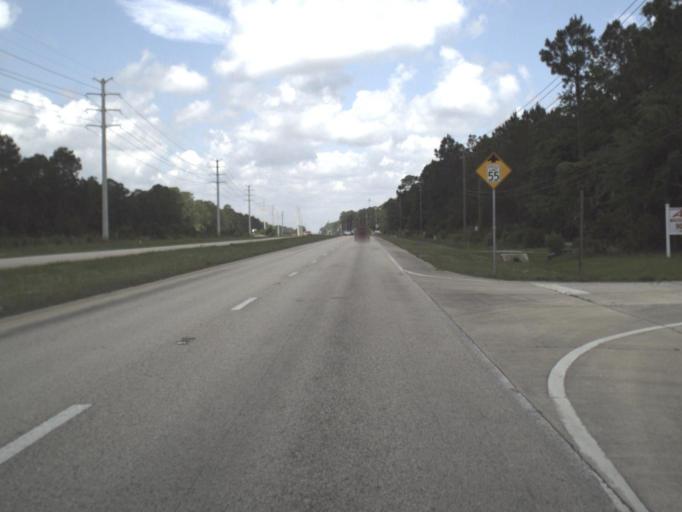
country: US
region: Florida
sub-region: Saint Johns County
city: Palm Valley
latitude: 30.0678
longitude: -81.4417
